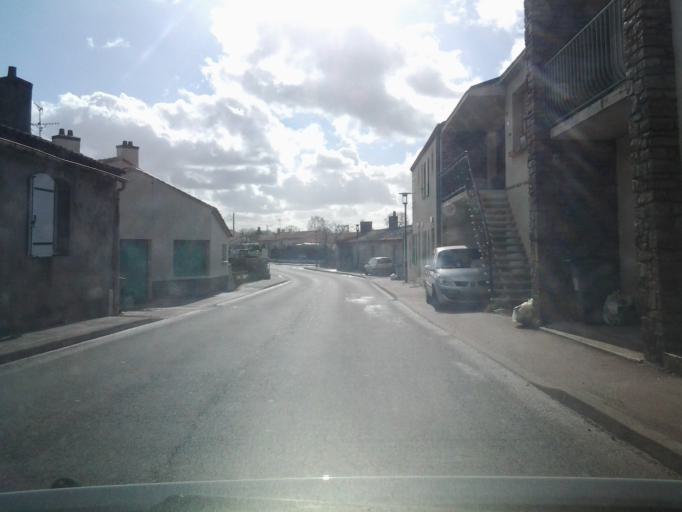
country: FR
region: Pays de la Loire
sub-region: Departement de la Vendee
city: Les Clouzeaux
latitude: 46.6285
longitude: -1.5086
